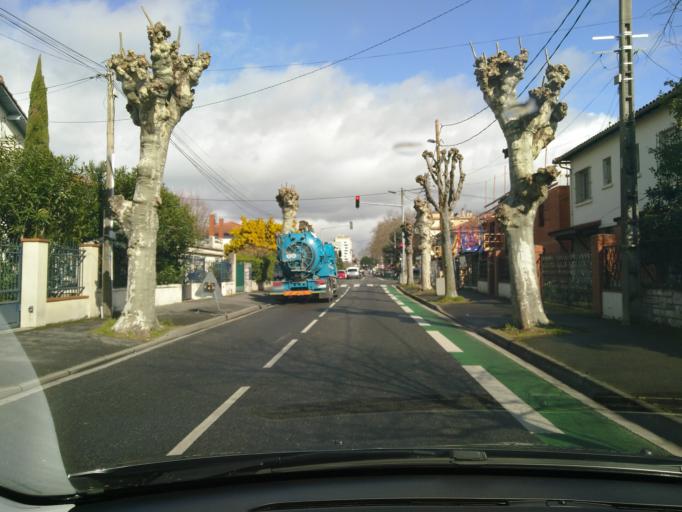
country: FR
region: Midi-Pyrenees
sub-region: Departement de la Haute-Garonne
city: Toulouse
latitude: 43.5780
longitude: 1.4574
